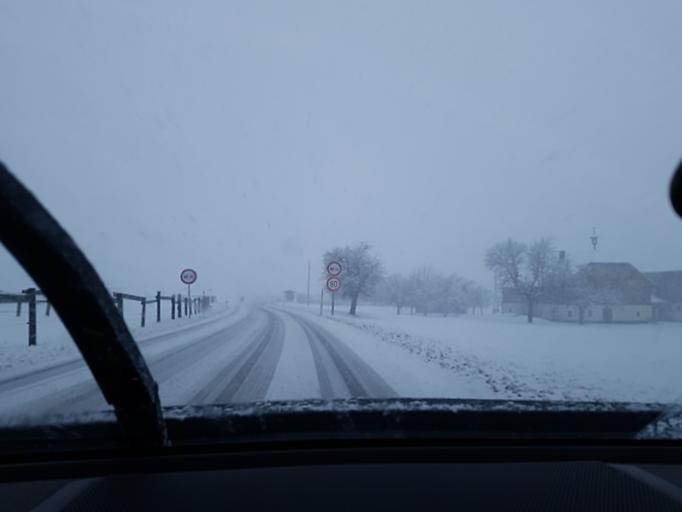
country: AT
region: Salzburg
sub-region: Politischer Bezirk Hallein
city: Abtenau
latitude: 47.5616
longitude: 13.3741
